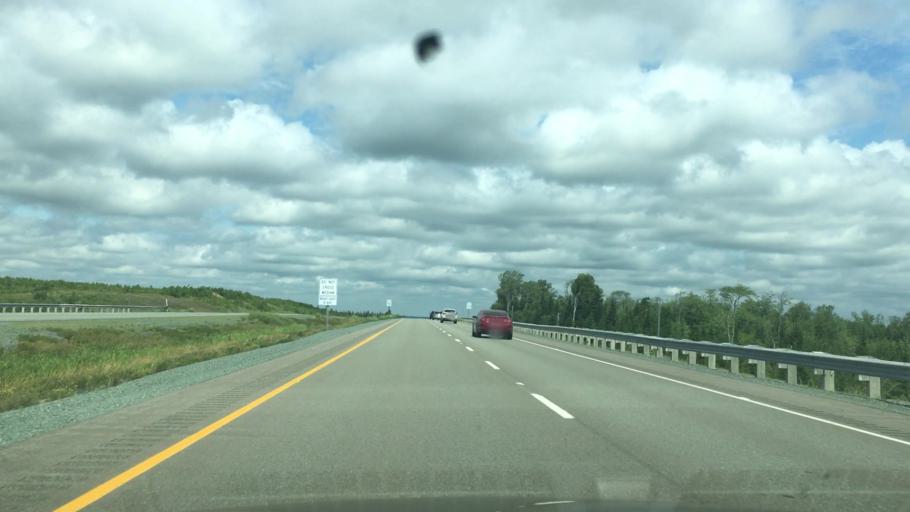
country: CA
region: Nova Scotia
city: Oxford
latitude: 45.6210
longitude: -63.7419
